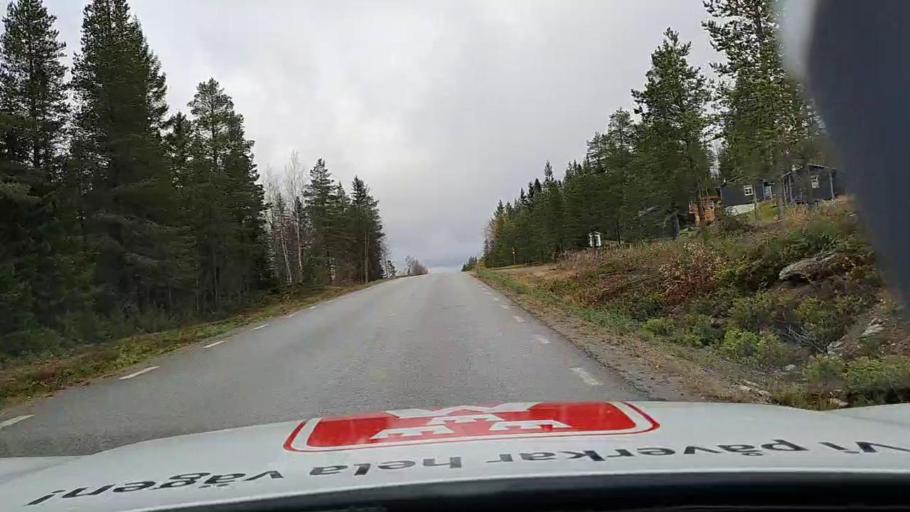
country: SE
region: Jaemtland
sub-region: Bergs Kommun
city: Hoverberg
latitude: 63.0314
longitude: 14.0510
